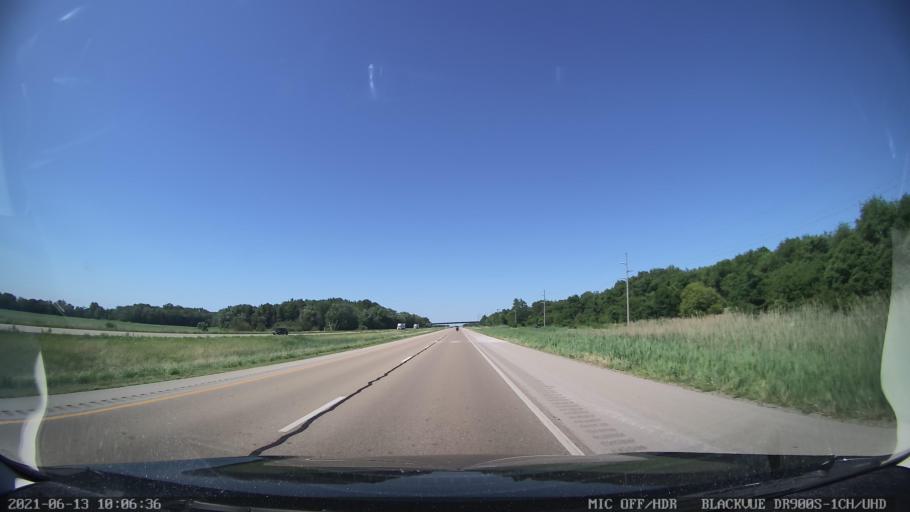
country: US
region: Illinois
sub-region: Logan County
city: Atlanta
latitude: 40.2259
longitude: -89.2721
